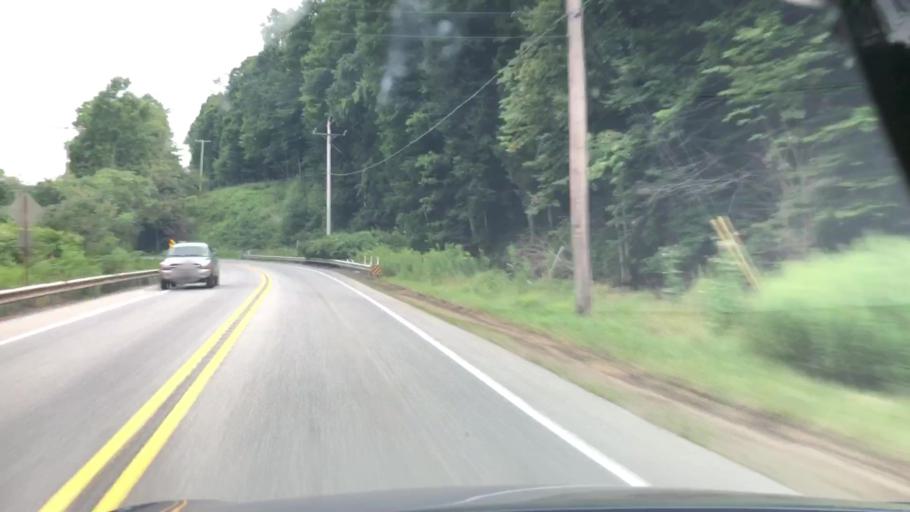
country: US
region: Pennsylvania
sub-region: Venango County
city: Hasson Heights
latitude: 41.4900
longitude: -79.7000
